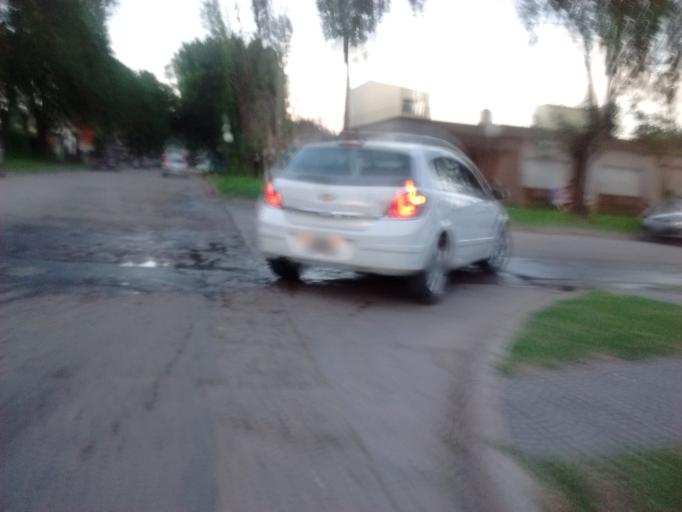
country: AR
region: Santa Fe
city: Funes
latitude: -32.9122
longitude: -60.8125
